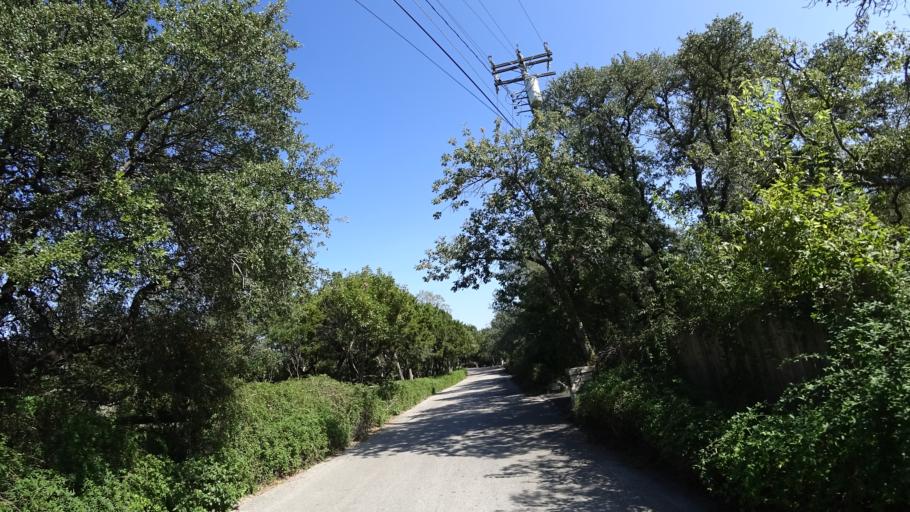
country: US
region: Texas
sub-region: Travis County
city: West Lake Hills
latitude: 30.3004
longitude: -97.8077
